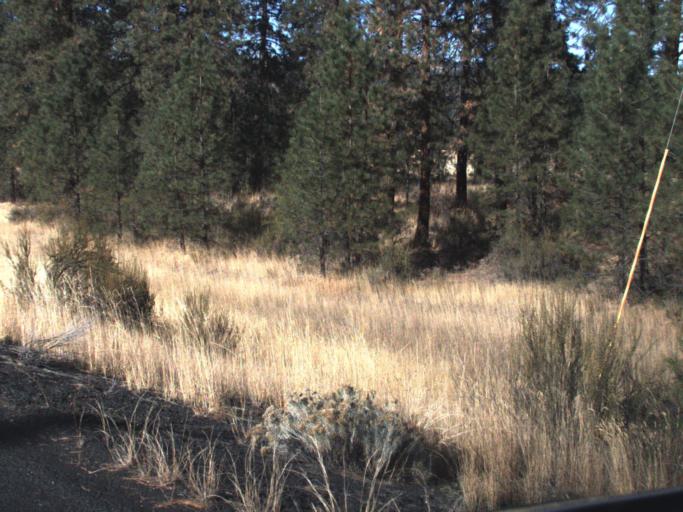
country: US
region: Washington
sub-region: Lincoln County
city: Davenport
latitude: 47.9036
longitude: -118.3031
